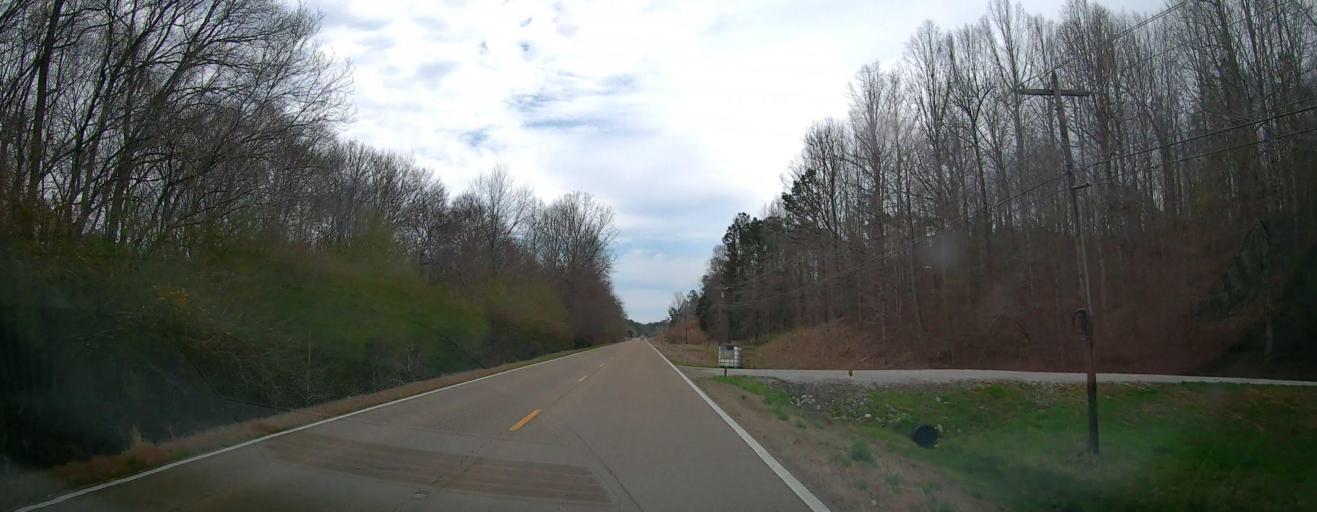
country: US
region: Mississippi
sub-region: Itawamba County
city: Fulton
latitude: 34.2566
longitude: -88.3145
